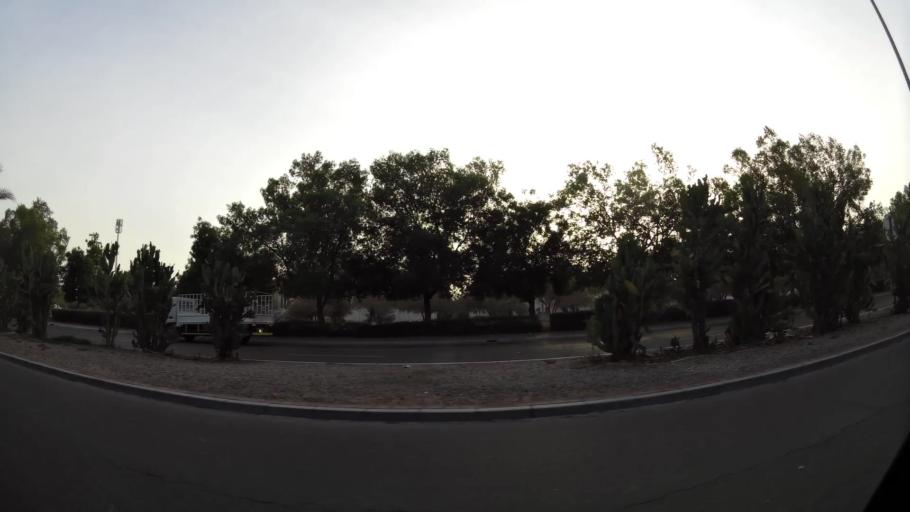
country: AE
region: Abu Dhabi
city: Al Ain
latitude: 24.2495
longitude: 55.7198
